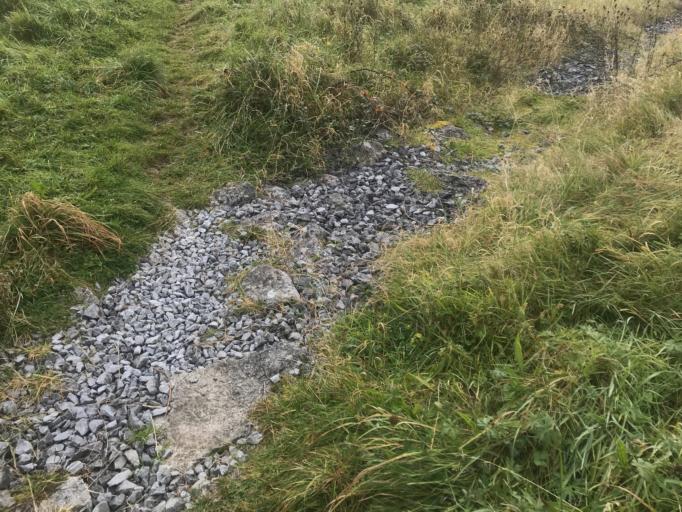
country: IE
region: Connaught
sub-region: County Galway
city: Gaillimh
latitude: 53.2958
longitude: -9.0453
